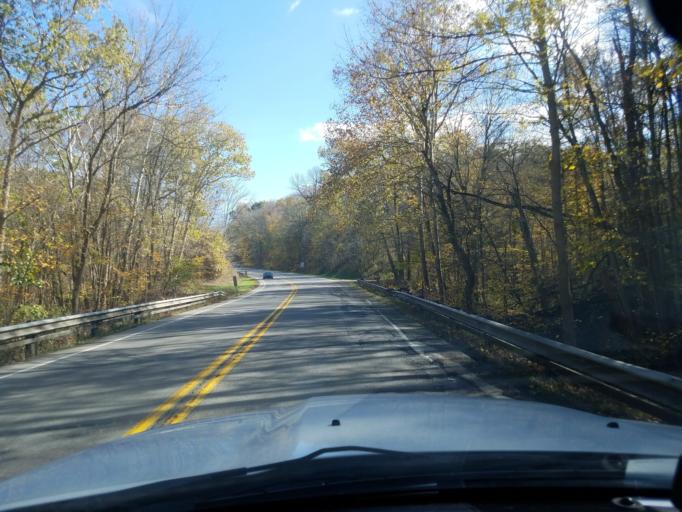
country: US
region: Indiana
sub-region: Ripley County
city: Versailles
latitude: 39.0645
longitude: -85.2214
